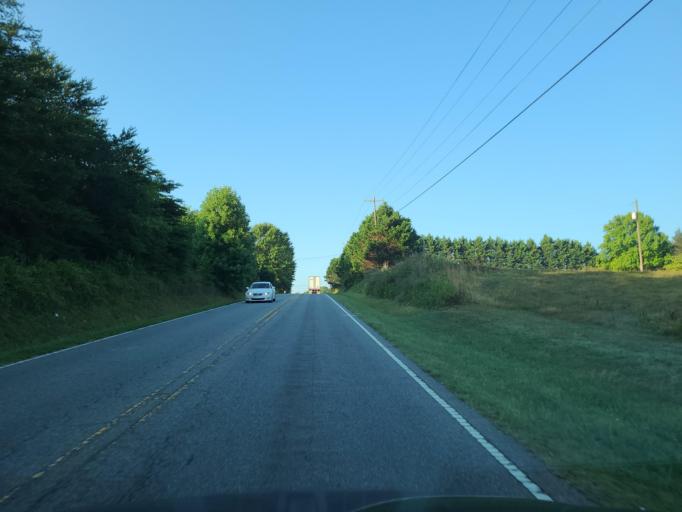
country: US
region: North Carolina
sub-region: Catawba County
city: Mountain View
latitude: 35.6410
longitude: -81.3816
